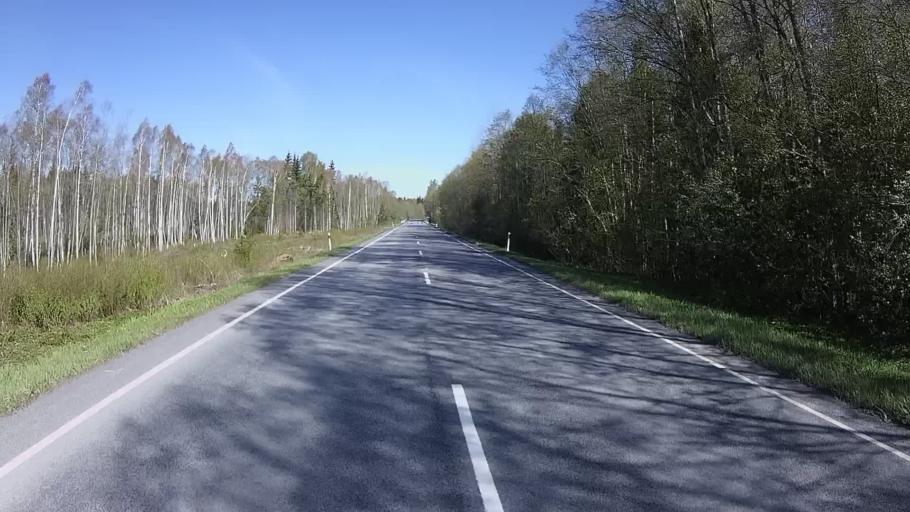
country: EE
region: Raplamaa
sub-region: Jaervakandi vald
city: Jarvakandi
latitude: 58.8207
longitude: 24.8000
